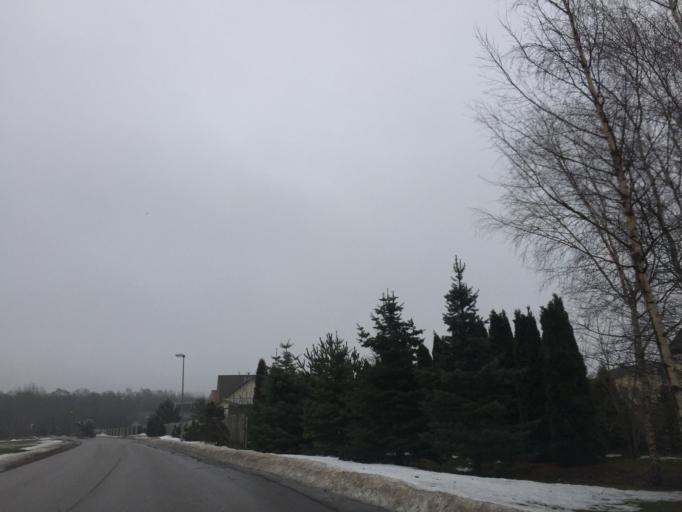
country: EE
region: Saare
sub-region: Kuressaare linn
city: Kuressaare
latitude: 58.2617
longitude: 22.5159
